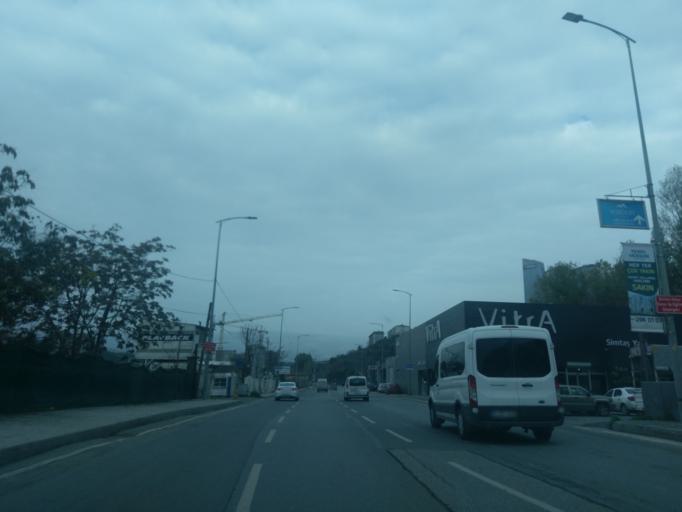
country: TR
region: Istanbul
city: Sisli
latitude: 41.0919
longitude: 28.9848
